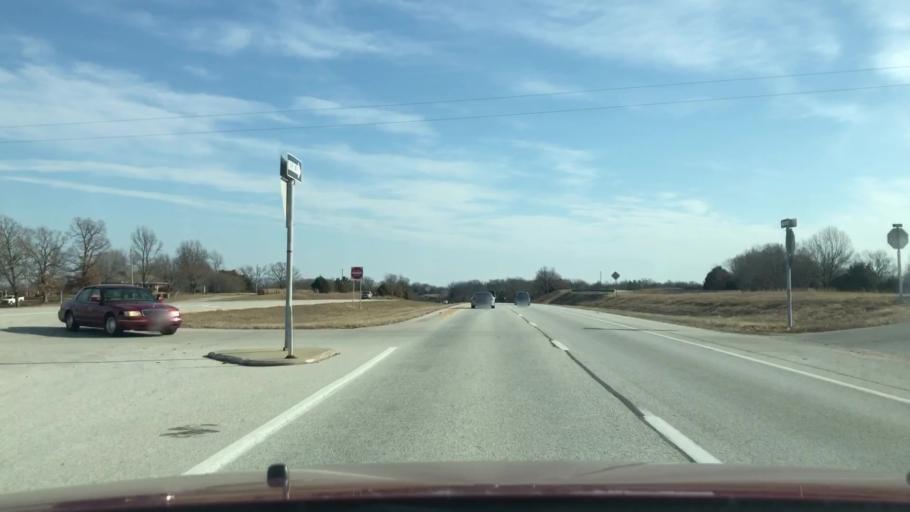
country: US
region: Missouri
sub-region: Webster County
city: Seymour
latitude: 37.1604
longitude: -92.9013
